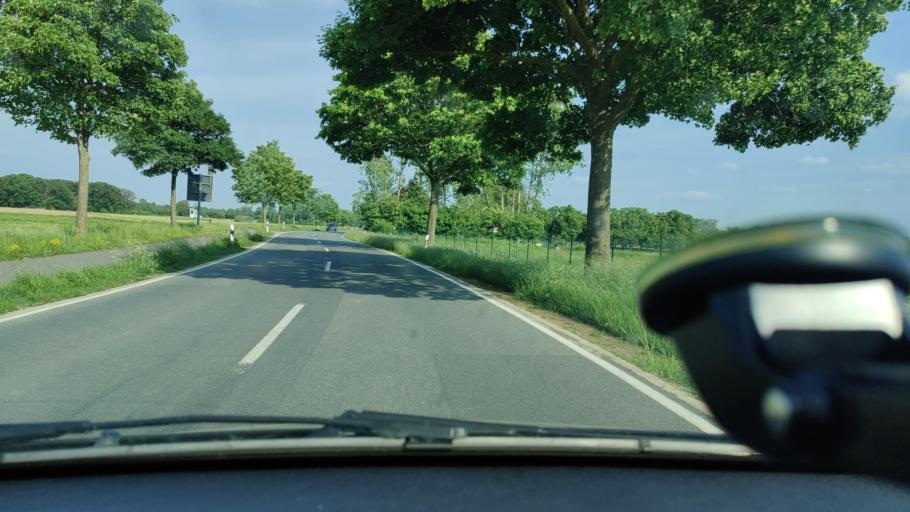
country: DE
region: North Rhine-Westphalia
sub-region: Regierungsbezirk Dusseldorf
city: Uedem
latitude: 51.6297
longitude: 6.2914
